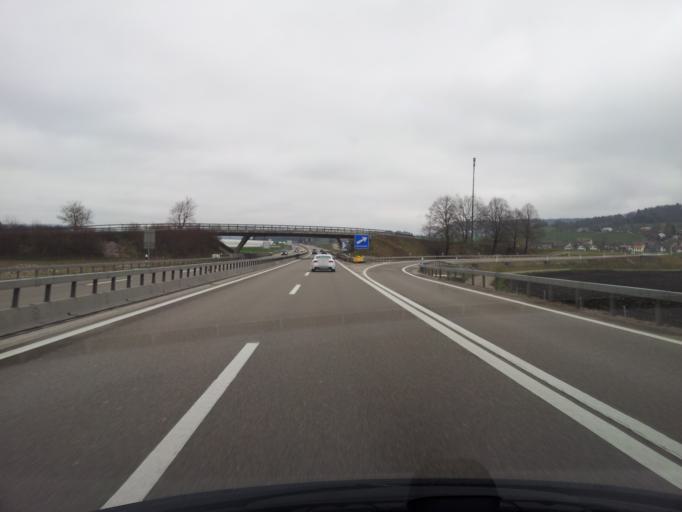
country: CH
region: Zurich
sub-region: Bezirk Andelfingen
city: Marthalen
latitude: 47.6449
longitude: 8.6518
